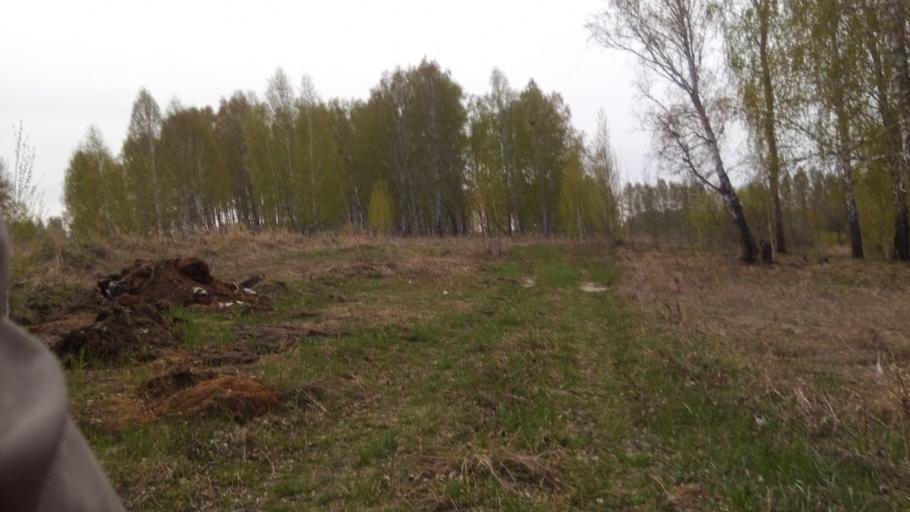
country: RU
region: Chelyabinsk
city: Timiryazevskiy
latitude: 55.0009
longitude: 60.8520
